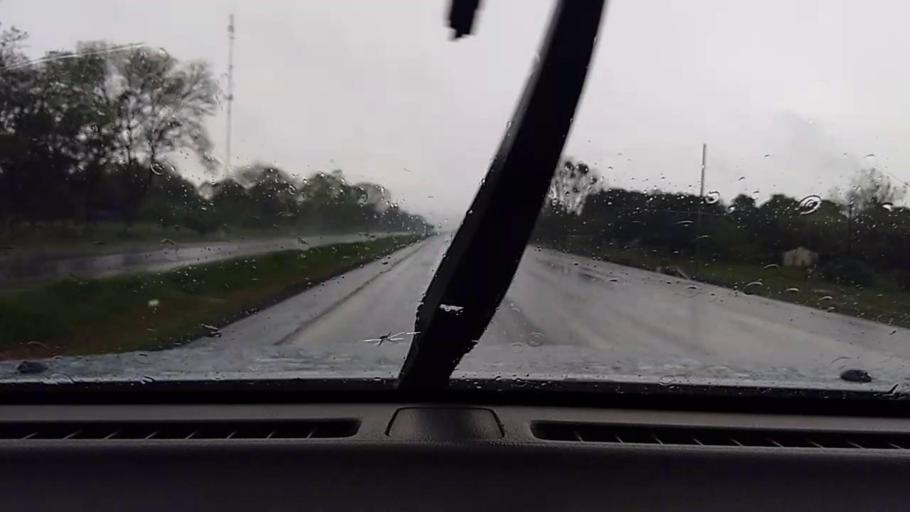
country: PY
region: Caaguazu
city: Repatriacion
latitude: -25.4526
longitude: -55.9056
